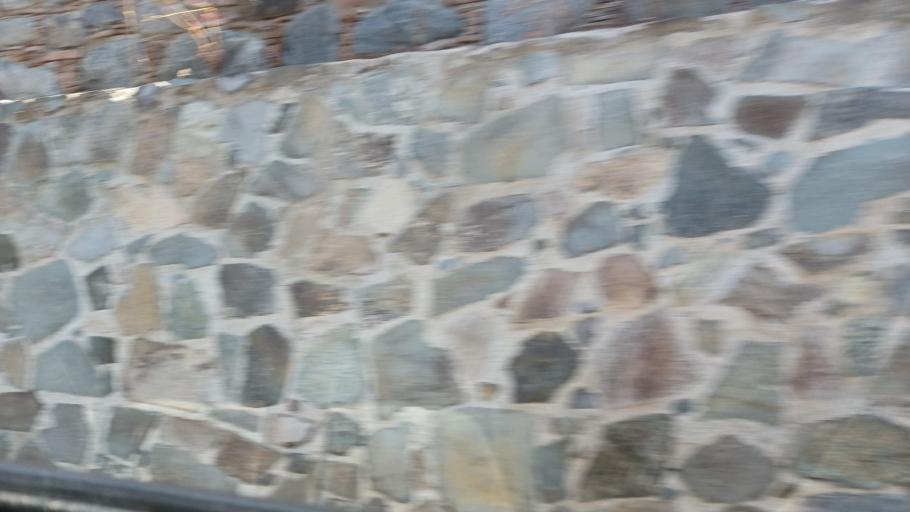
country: CY
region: Lefkosia
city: Lefka
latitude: 35.0605
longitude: 32.8876
